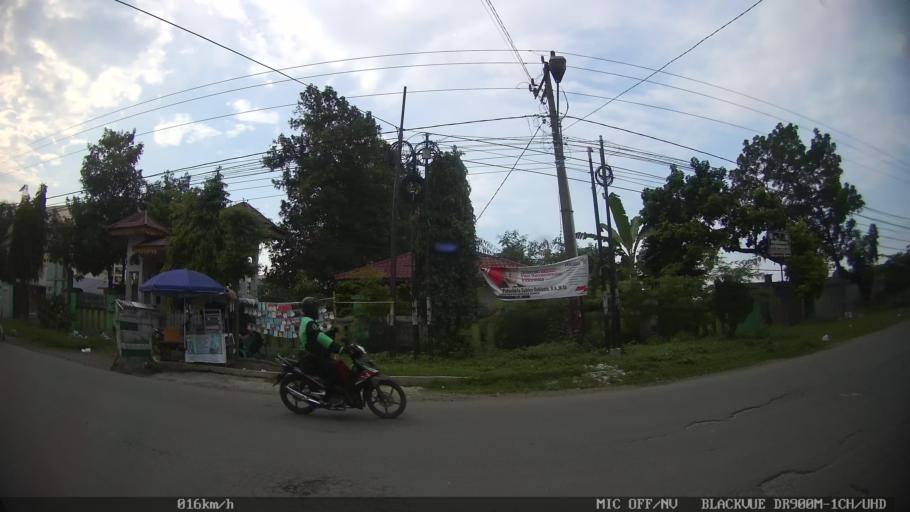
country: ID
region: North Sumatra
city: Medan
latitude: 3.6062
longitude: 98.7101
